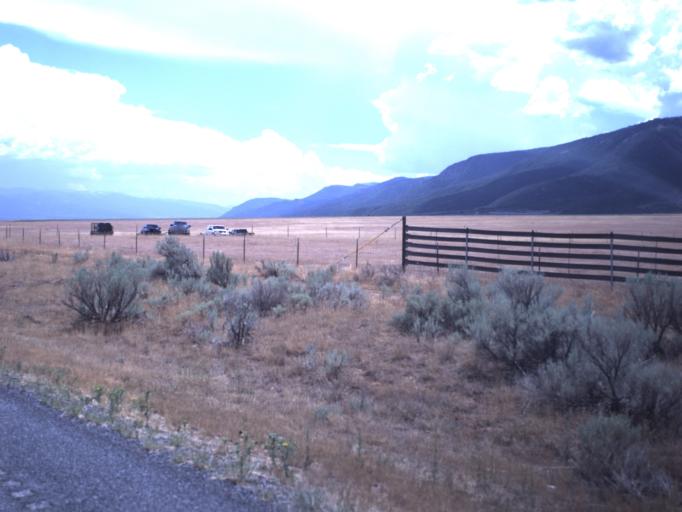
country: US
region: Utah
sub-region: Sanpete County
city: Fountain Green
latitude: 39.6636
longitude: -111.6575
